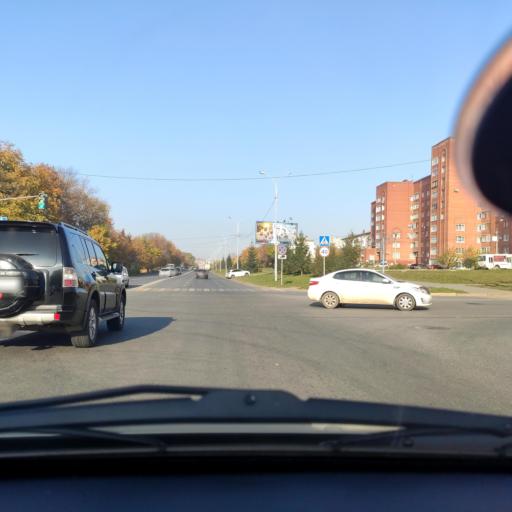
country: RU
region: Bashkortostan
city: Ufa
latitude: 54.8038
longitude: 56.1113
